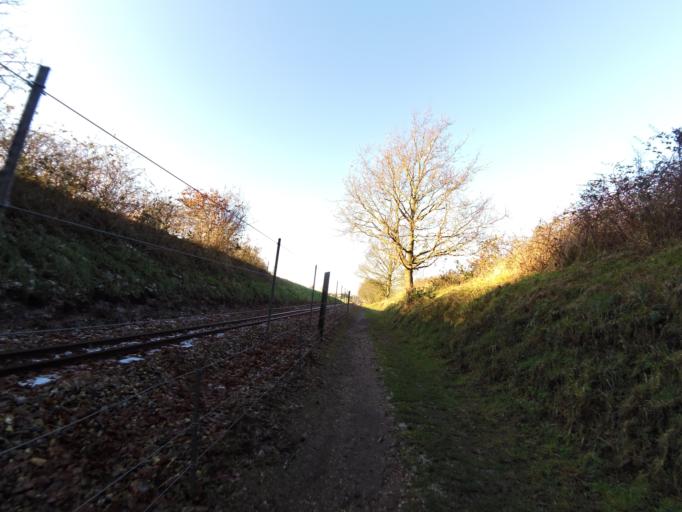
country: GB
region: England
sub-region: Norfolk
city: Aylsham
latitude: 52.7858
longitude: 1.2702
